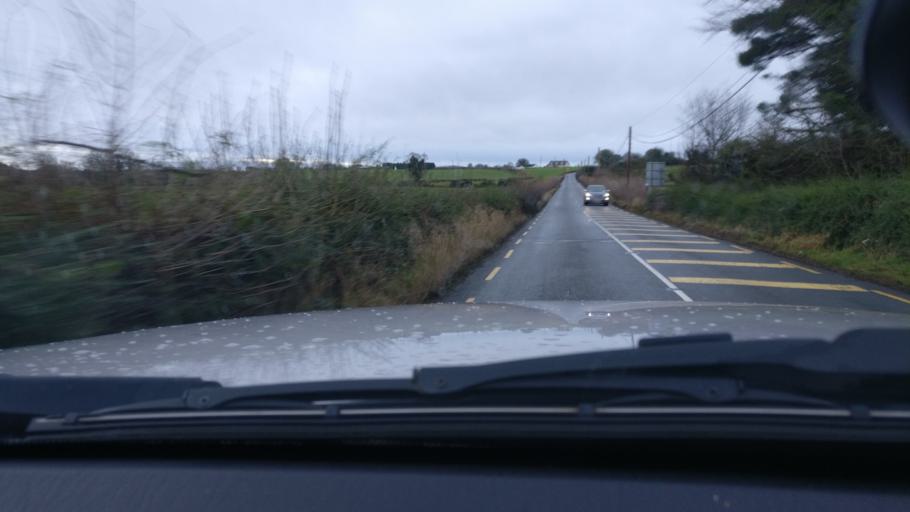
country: IE
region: Leinster
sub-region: An Longfort
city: Granard
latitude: 53.7963
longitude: -7.3905
